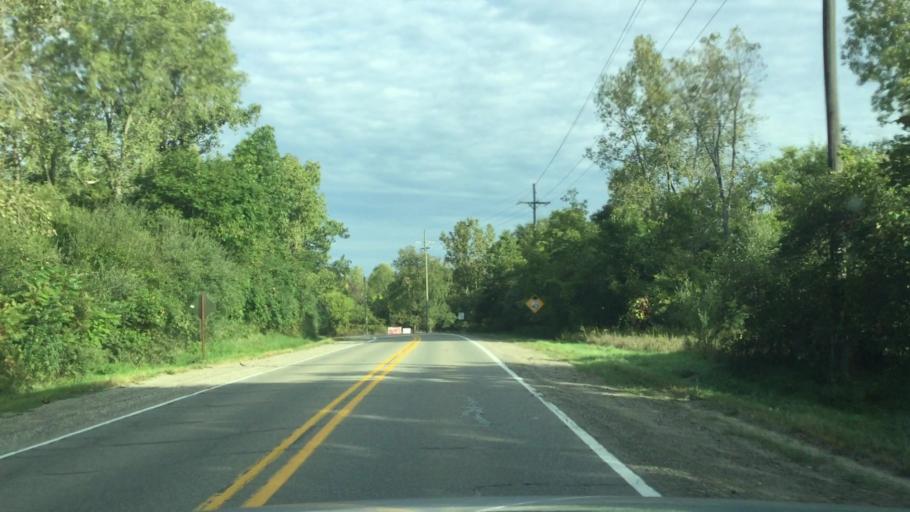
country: US
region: Michigan
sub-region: Livingston County
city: Brighton
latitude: 42.5193
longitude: -83.8555
